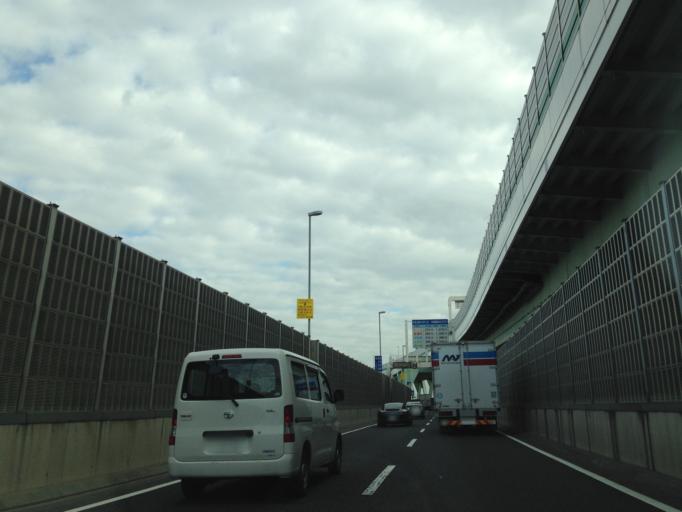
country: JP
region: Saitama
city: Kawaguchi
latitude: 35.7571
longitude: 139.7453
